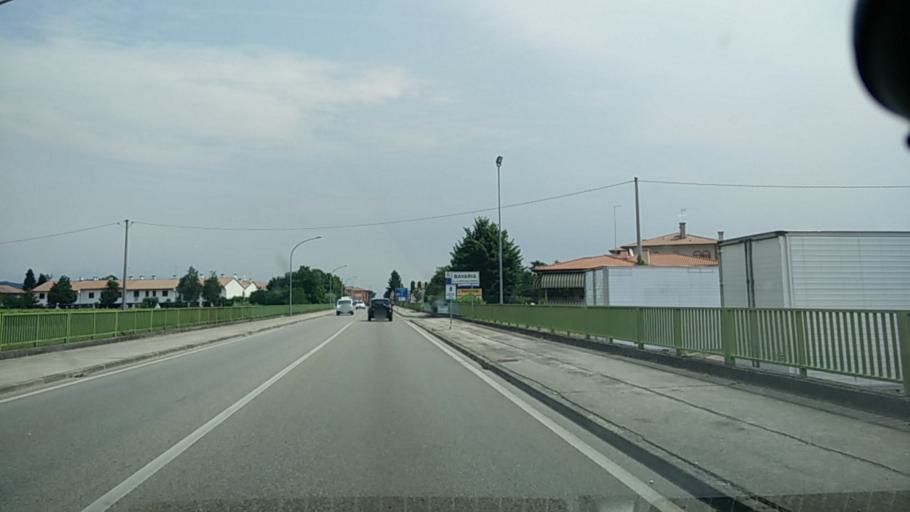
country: IT
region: Veneto
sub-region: Provincia di Treviso
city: Nervesa della Battaglia
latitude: 45.8024
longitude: 12.1849
